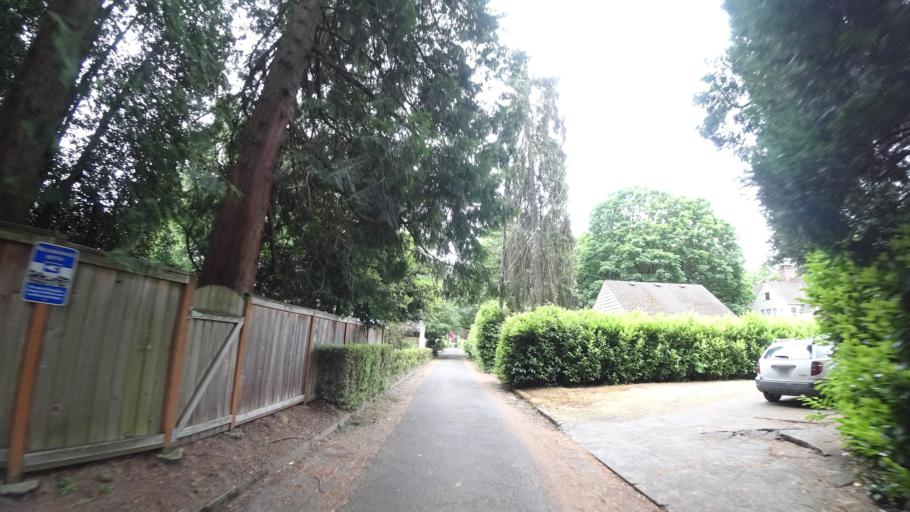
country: US
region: Oregon
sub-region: Clackamas County
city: Milwaukie
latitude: 45.4572
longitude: -122.6511
